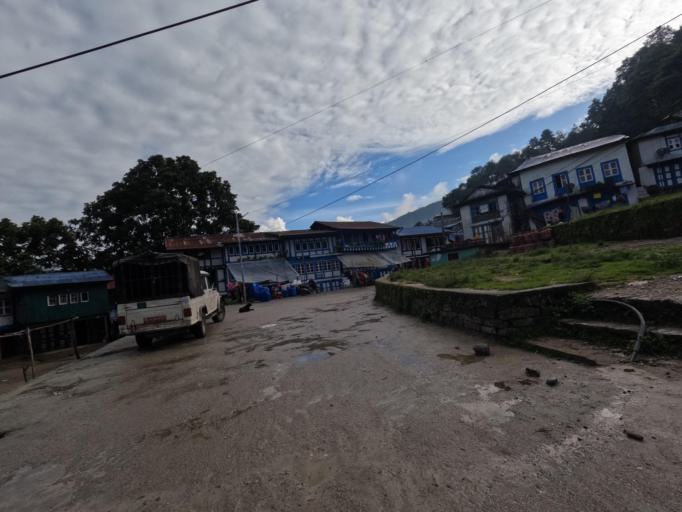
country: NP
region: Eastern Region
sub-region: Sagarmatha Zone
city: Namche Bazar
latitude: 27.4932
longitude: 86.5817
